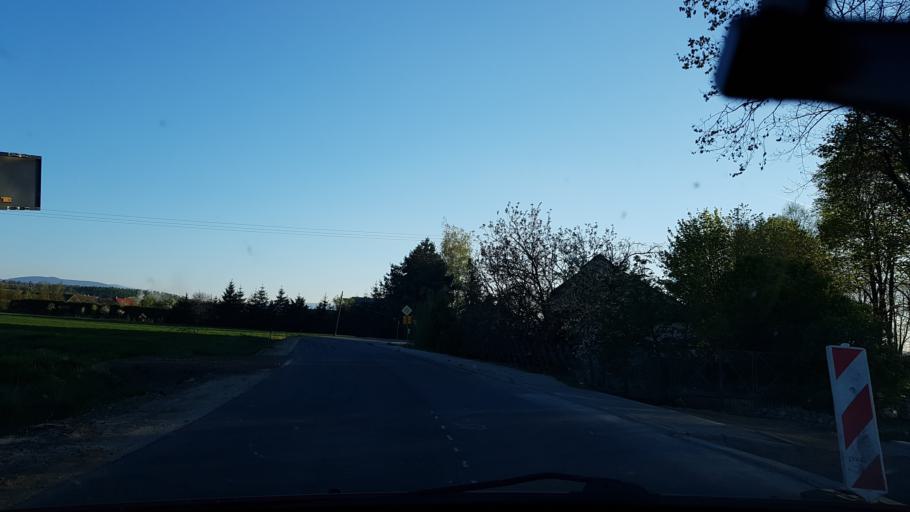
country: CZ
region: Olomoucky
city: Vidnava
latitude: 50.4223
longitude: 17.2295
